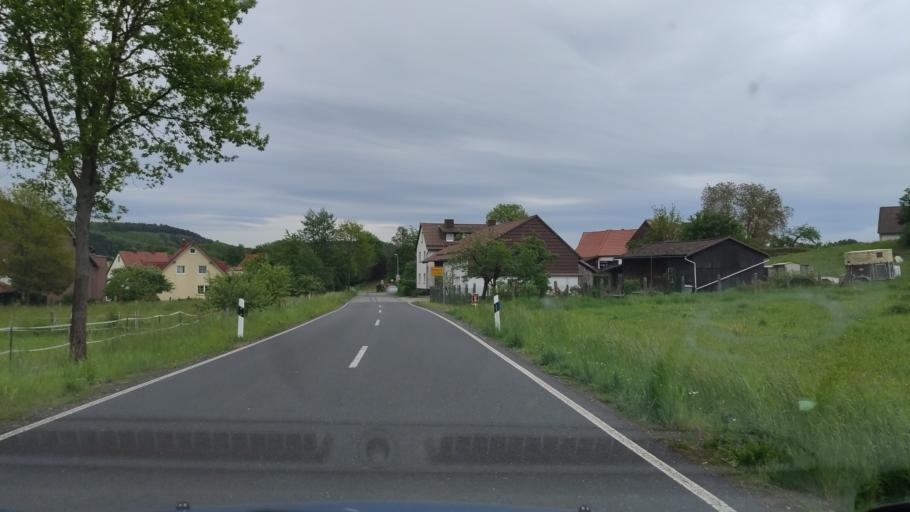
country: DE
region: Lower Saxony
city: Hardegsen
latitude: 51.6916
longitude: 9.8004
